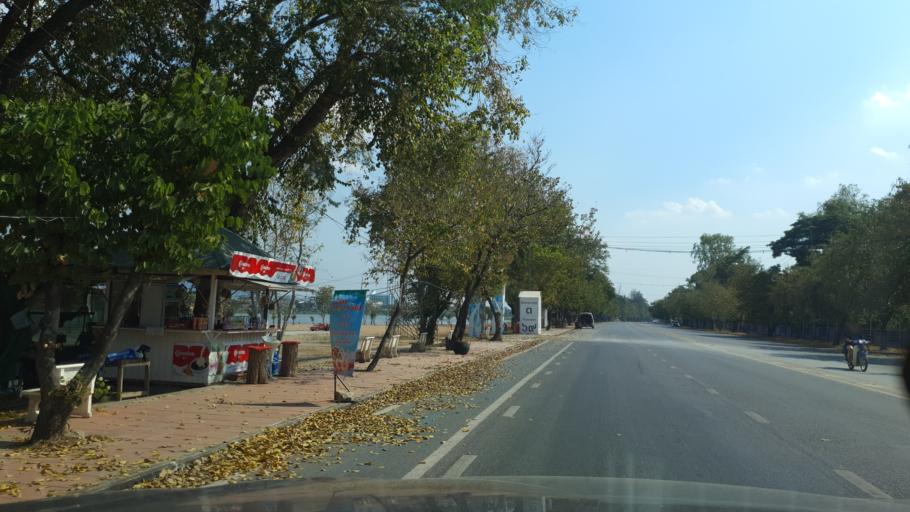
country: TH
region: Tak
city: Tak
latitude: 16.8802
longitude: 99.1147
